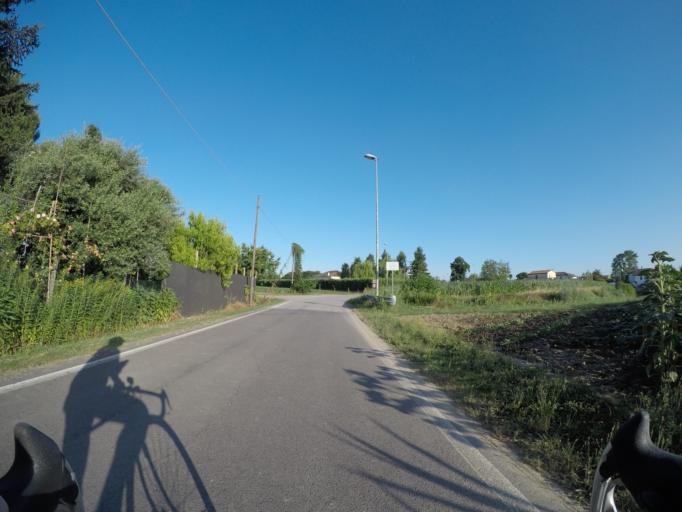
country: IT
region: Veneto
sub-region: Provincia di Rovigo
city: Villamarzana
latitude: 45.0243
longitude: 11.6765
